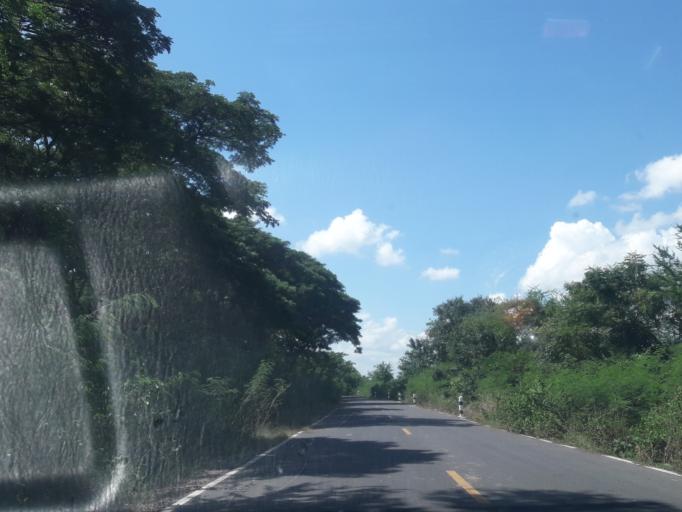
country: TH
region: Lop Buri
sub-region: Amphoe Tha Luang
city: Tha Luang
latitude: 15.0698
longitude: 101.0343
